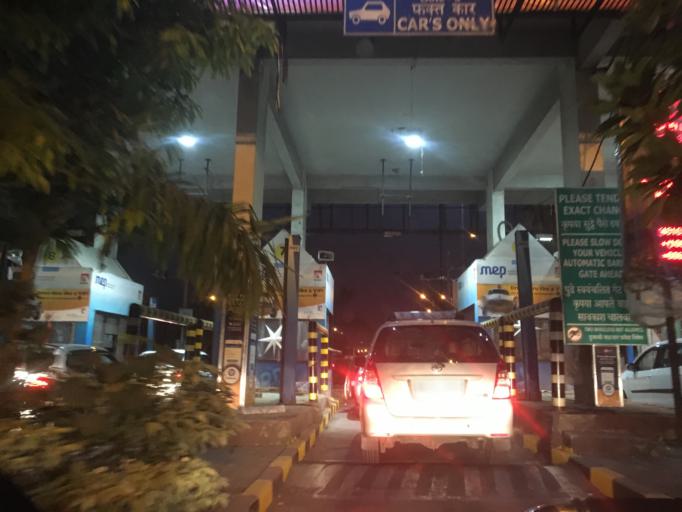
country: IN
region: Maharashtra
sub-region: Thane
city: Airoli
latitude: 19.1533
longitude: 72.9659
